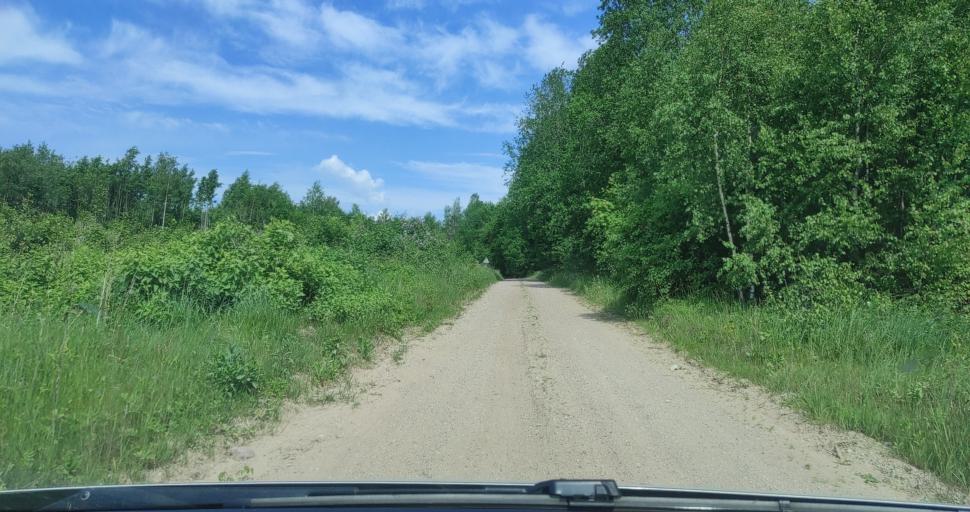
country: LV
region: Kuldigas Rajons
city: Kuldiga
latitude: 56.8589
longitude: 21.9084
